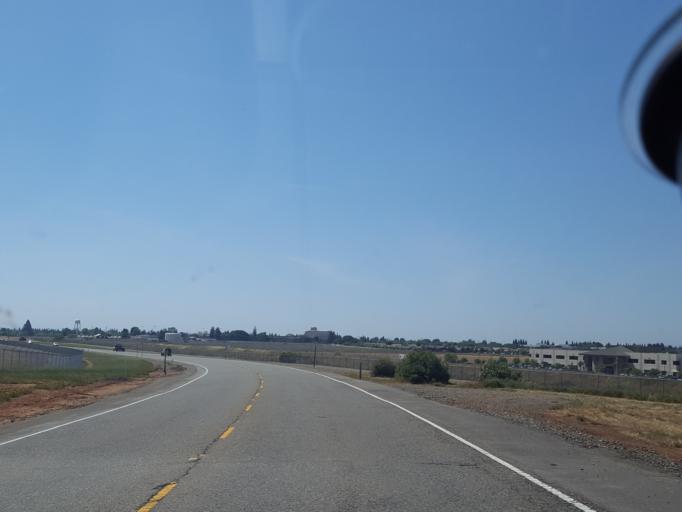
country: US
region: California
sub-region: Sacramento County
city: Rancho Cordova
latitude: 38.5673
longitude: -121.2741
